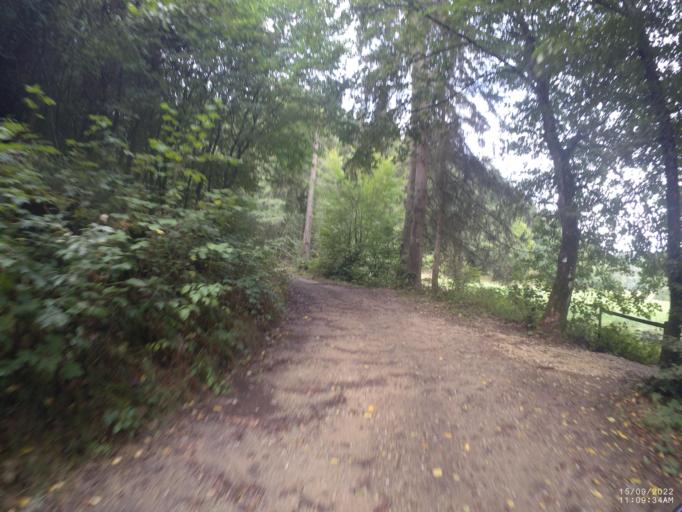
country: DE
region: Rheinland-Pfalz
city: Dankerath
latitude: 50.3135
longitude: 6.8047
